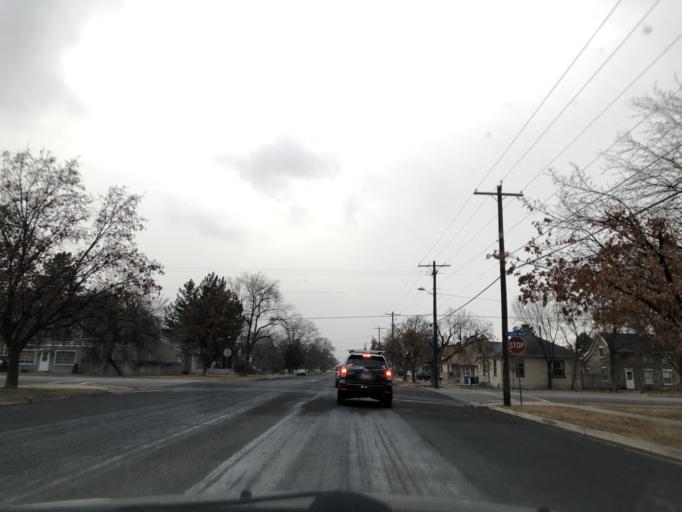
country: US
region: Utah
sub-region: Cache County
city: Logan
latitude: 41.7334
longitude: -111.8396
